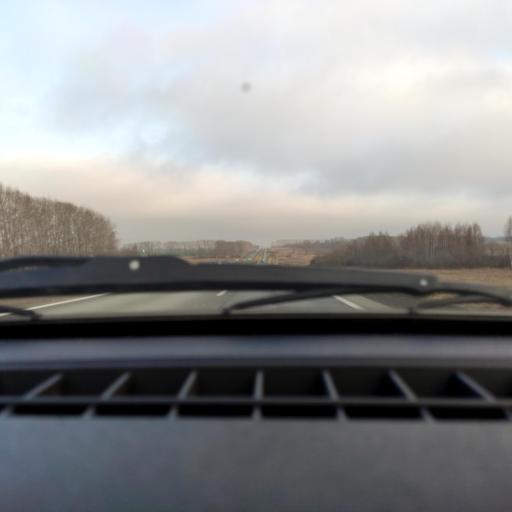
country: RU
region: Bashkortostan
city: Chishmy
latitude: 54.6651
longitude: 55.4205
